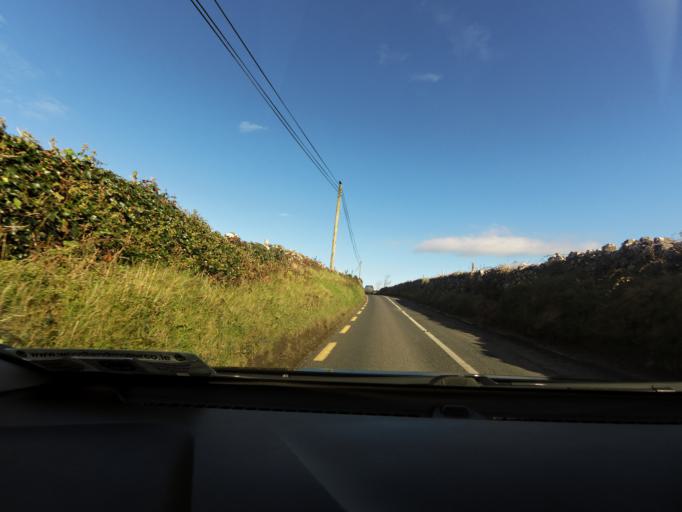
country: IE
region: Connaught
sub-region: County Galway
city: Moycullen
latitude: 53.4910
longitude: -9.0807
